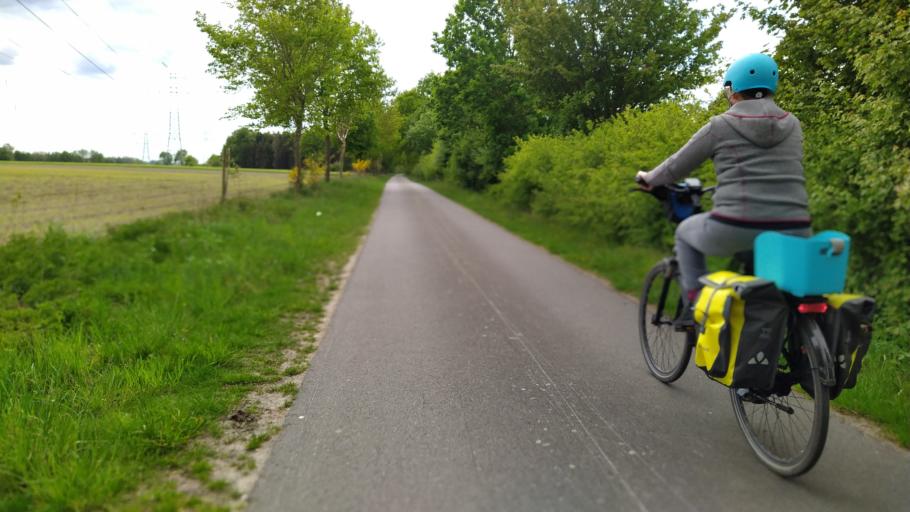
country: DE
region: Lower Saxony
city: Ahlerstedt
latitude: 53.3725
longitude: 9.3953
